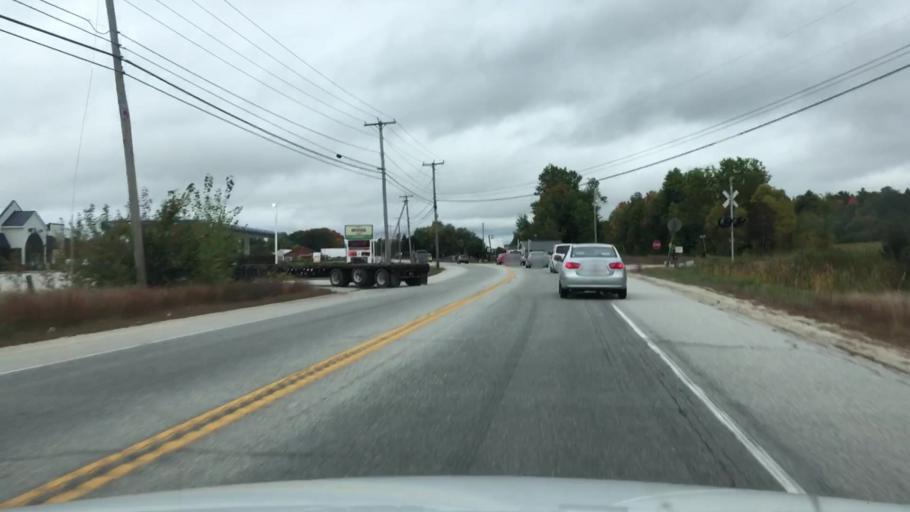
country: US
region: Maine
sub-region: Oxford County
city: South Paris
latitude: 44.1801
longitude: -70.5156
